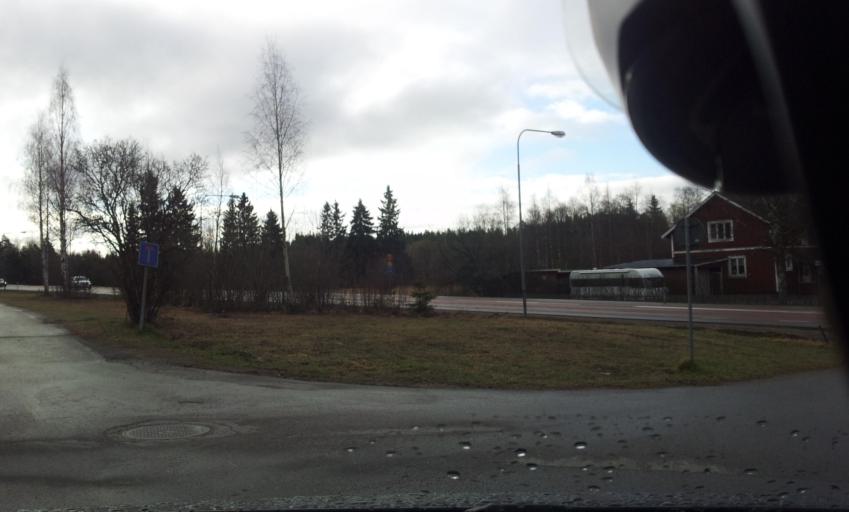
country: SE
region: Gaevleborg
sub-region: Ljusdals Kommun
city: Ljusdal
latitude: 61.8259
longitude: 16.1290
